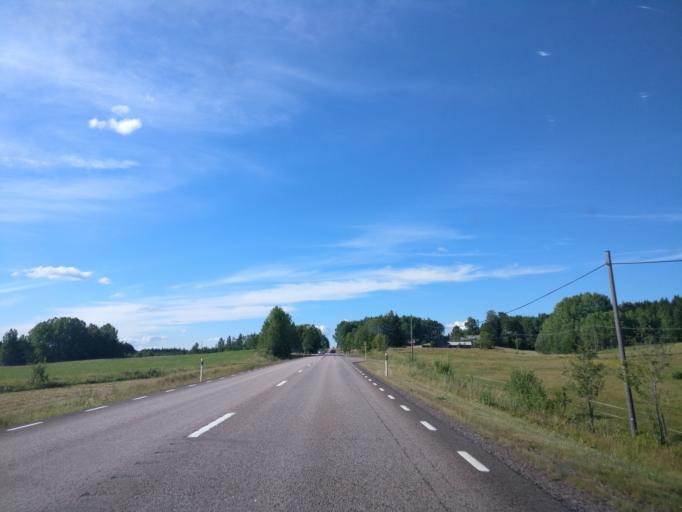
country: SE
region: Vaermland
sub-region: Karlstads Kommun
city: Edsvalla
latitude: 59.5790
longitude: 13.0179
